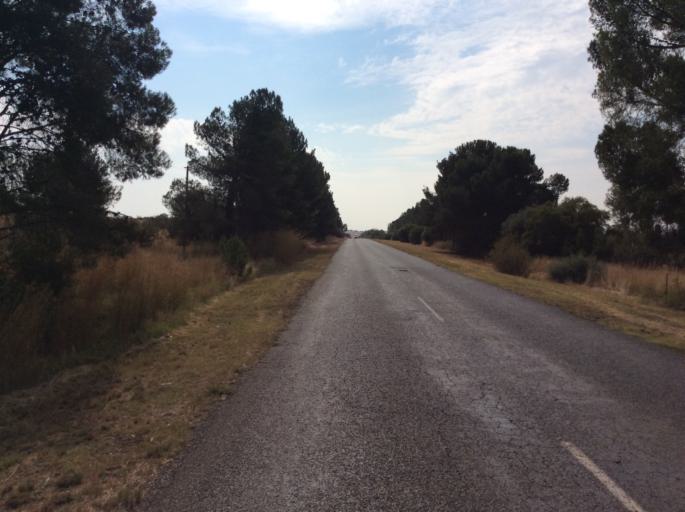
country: ZA
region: Orange Free State
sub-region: Xhariep District Municipality
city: Dewetsdorp
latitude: -29.5692
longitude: 26.6658
